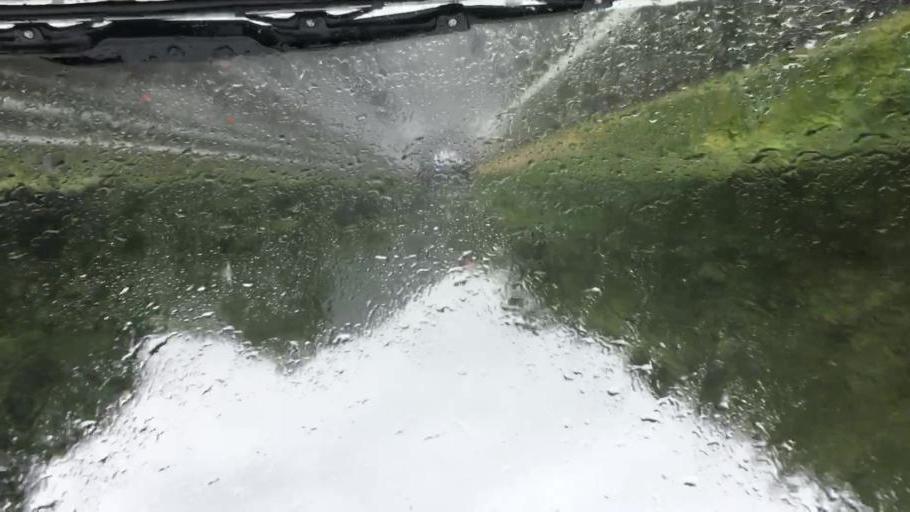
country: JP
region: Hokkaido
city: Otaru
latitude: 42.8457
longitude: 141.0563
